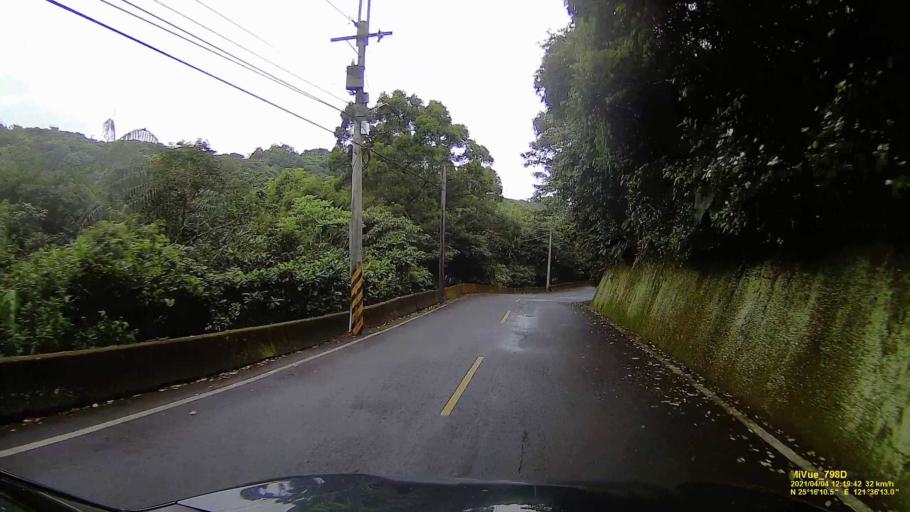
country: TW
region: Taiwan
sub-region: Keelung
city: Keelung
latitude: 25.2698
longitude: 121.6035
